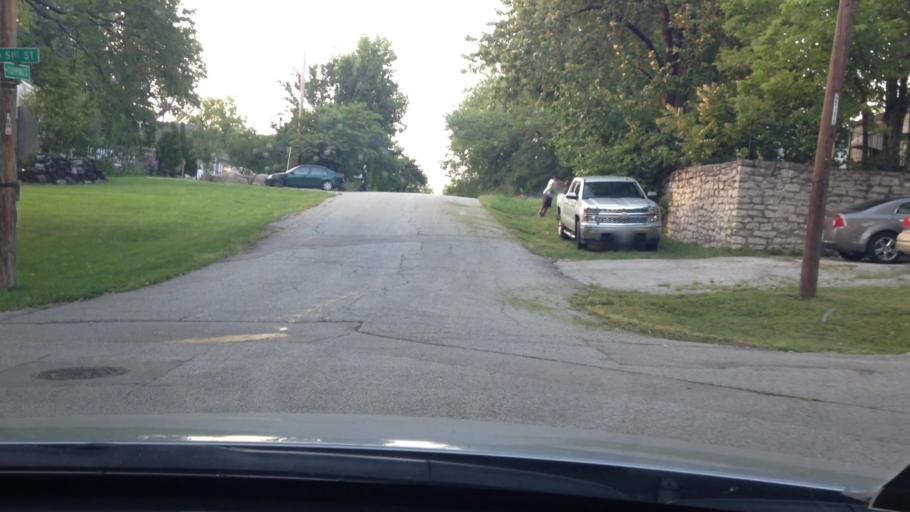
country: US
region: Missouri
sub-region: Clay County
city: Claycomo
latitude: 39.1860
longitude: -94.5120
